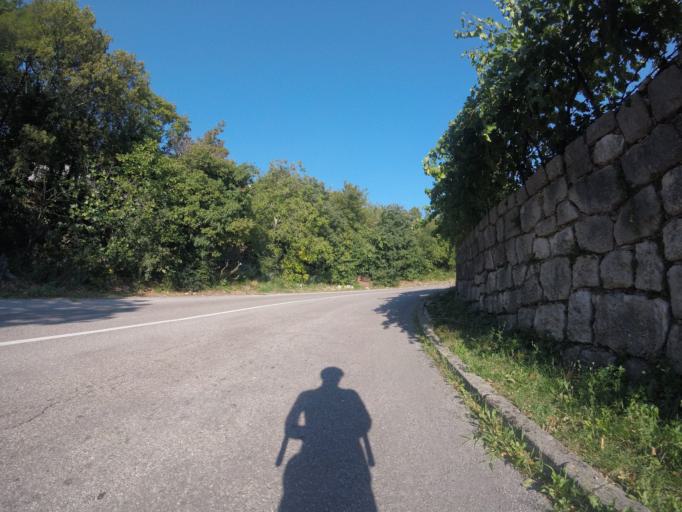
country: HR
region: Primorsko-Goranska
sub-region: Grad Crikvenica
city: Crikvenica
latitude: 45.2147
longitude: 14.7036
